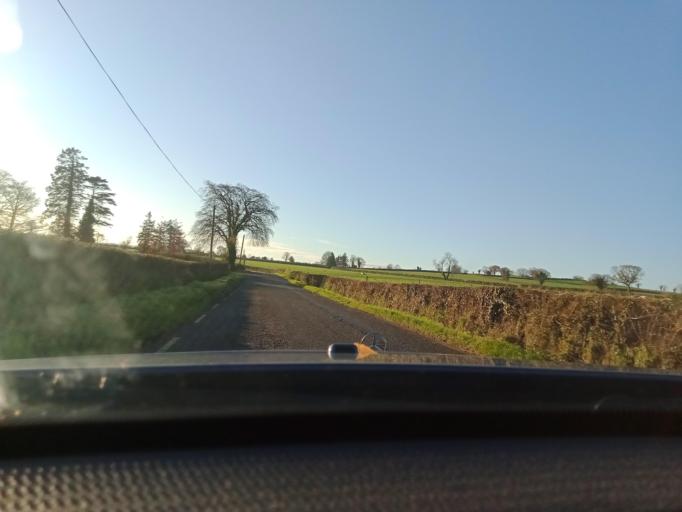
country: IE
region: Leinster
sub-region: Kilkenny
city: Callan
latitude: 52.4979
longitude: -7.3815
